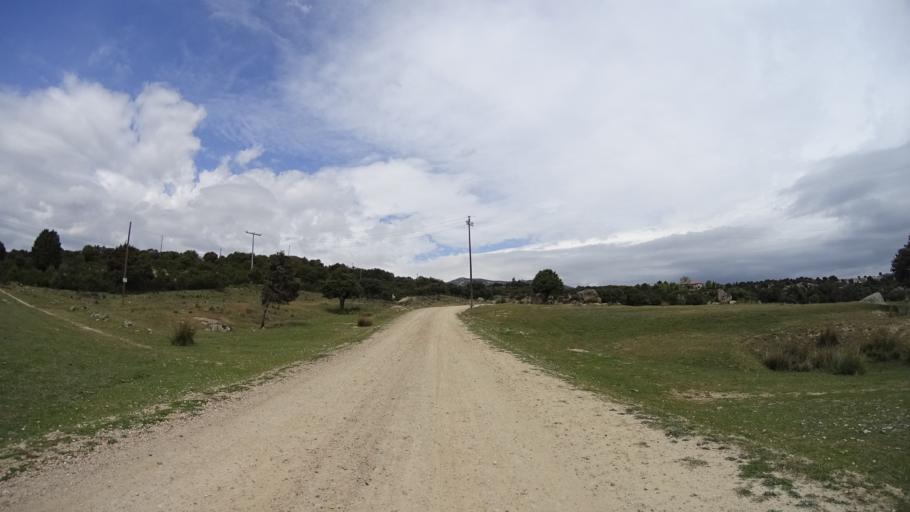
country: ES
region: Madrid
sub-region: Provincia de Madrid
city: Hoyo de Manzanares
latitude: 40.6184
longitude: -3.8814
